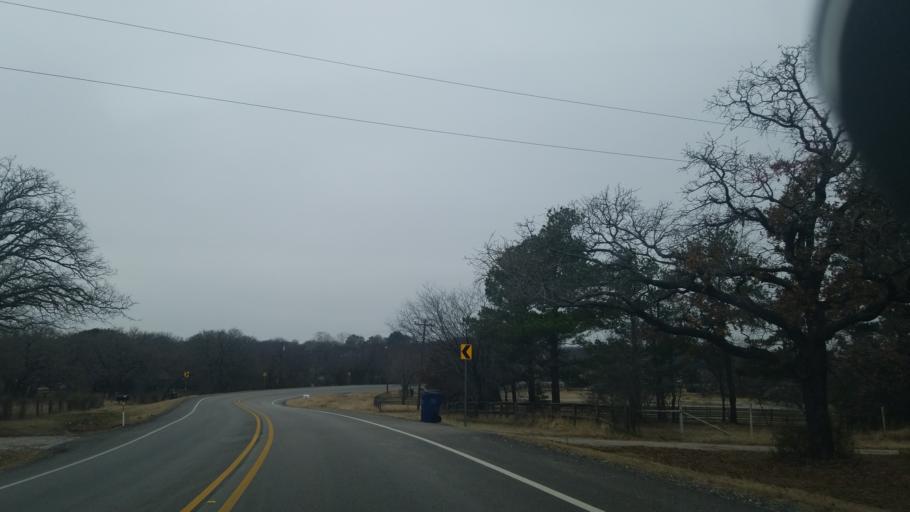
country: US
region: Texas
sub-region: Denton County
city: Argyle
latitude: 33.1324
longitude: -97.1462
